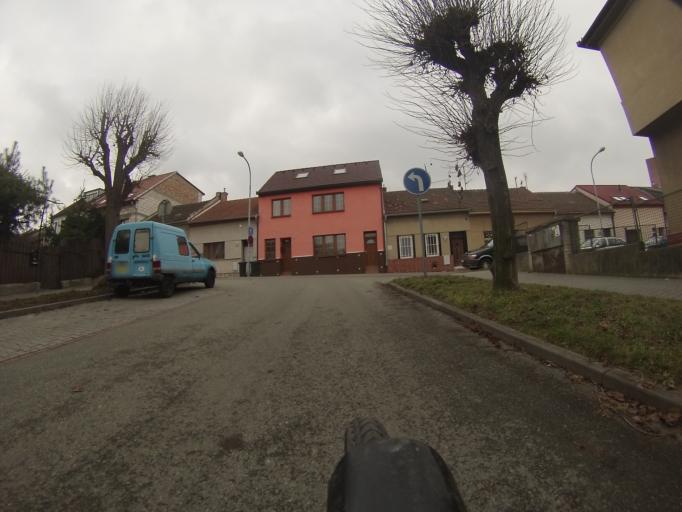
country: CZ
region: South Moravian
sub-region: Mesto Brno
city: Brno
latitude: 49.1968
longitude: 16.6533
